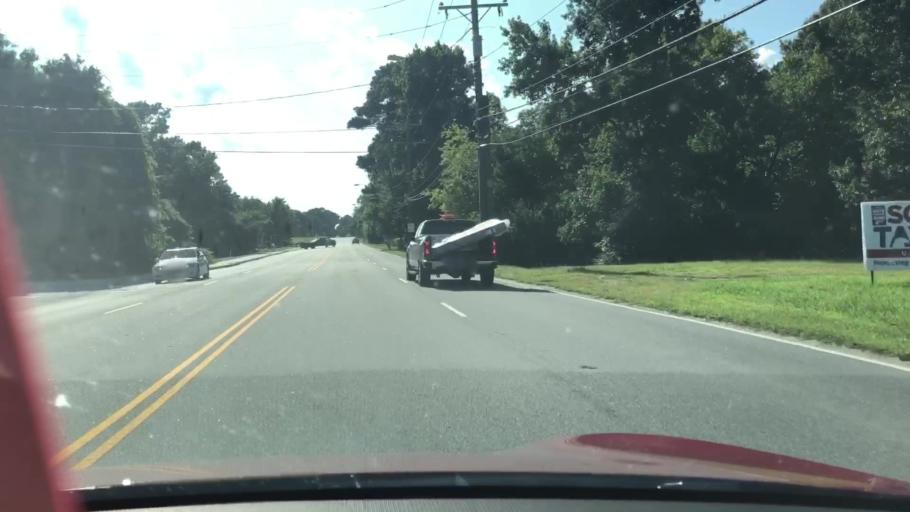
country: US
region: Virginia
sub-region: City of Virginia Beach
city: Virginia Beach
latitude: 36.8427
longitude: -76.0075
